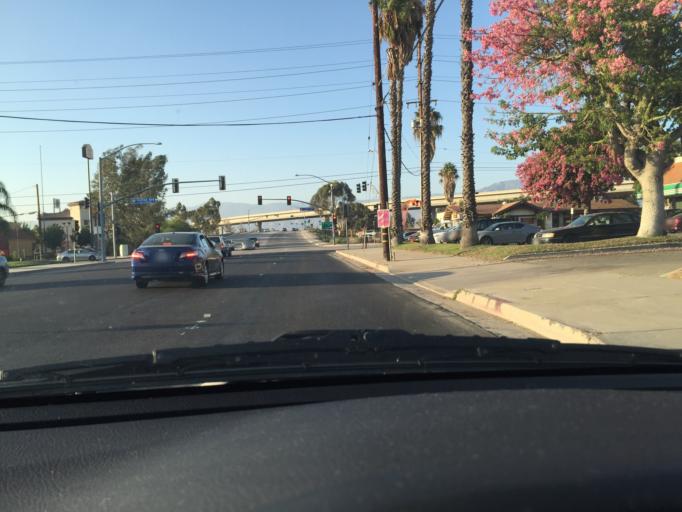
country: US
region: California
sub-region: San Bernardino County
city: Redlands
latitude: 34.0623
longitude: -117.2000
